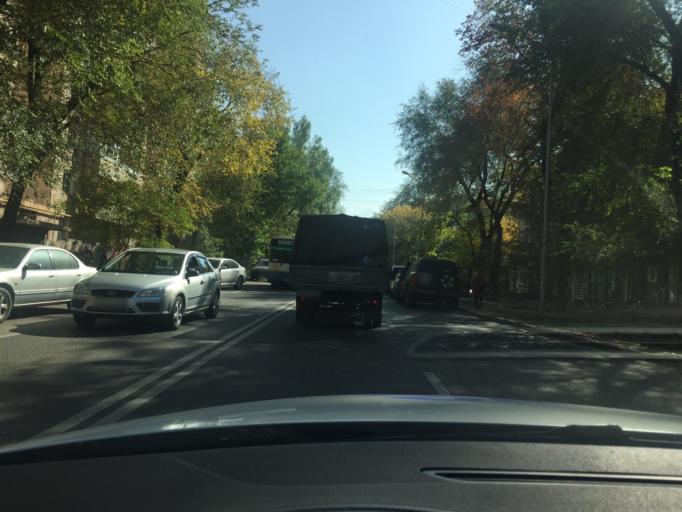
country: KZ
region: Almaty Qalasy
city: Almaty
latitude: 43.2519
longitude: 76.9116
